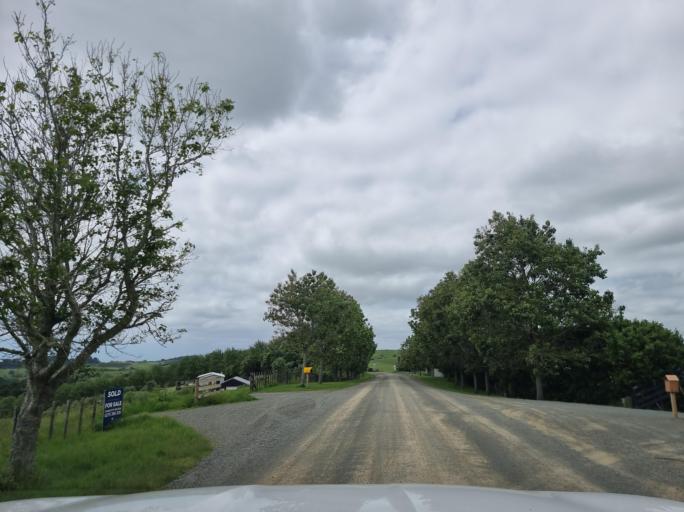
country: NZ
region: Auckland
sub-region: Auckland
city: Wellsford
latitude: -36.0937
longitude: 174.5319
